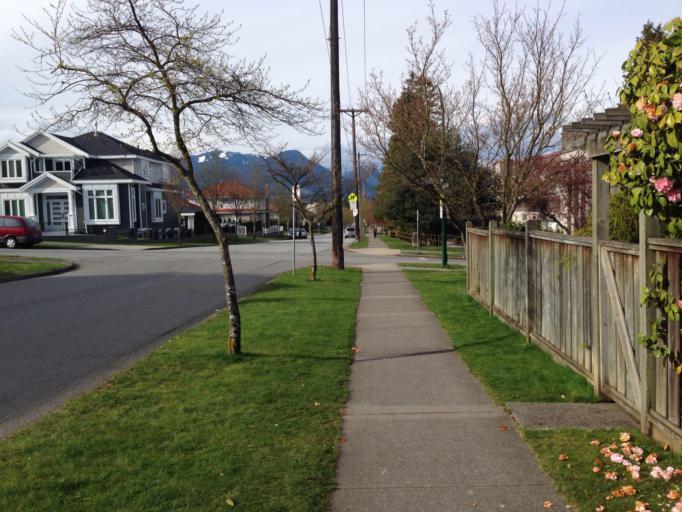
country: CA
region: British Columbia
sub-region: Fraser Valley Regional District
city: North Vancouver
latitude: 49.2710
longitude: -123.0389
